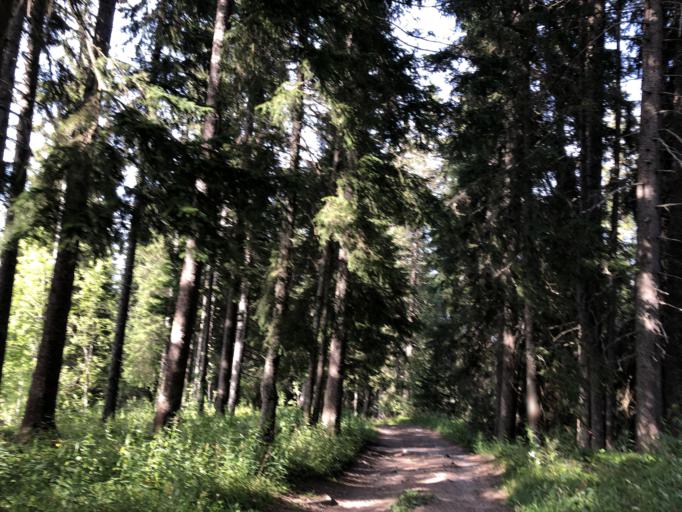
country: FR
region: Rhone-Alpes
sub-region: Departement de la Haute-Savoie
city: Combloux
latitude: 45.8719
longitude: 6.6608
